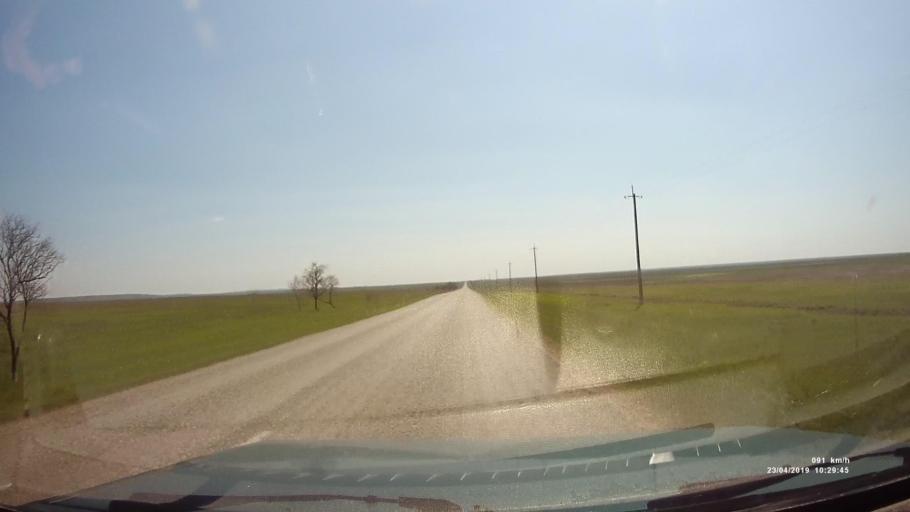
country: RU
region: Kalmykiya
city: Yashalta
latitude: 46.5967
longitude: 42.5321
